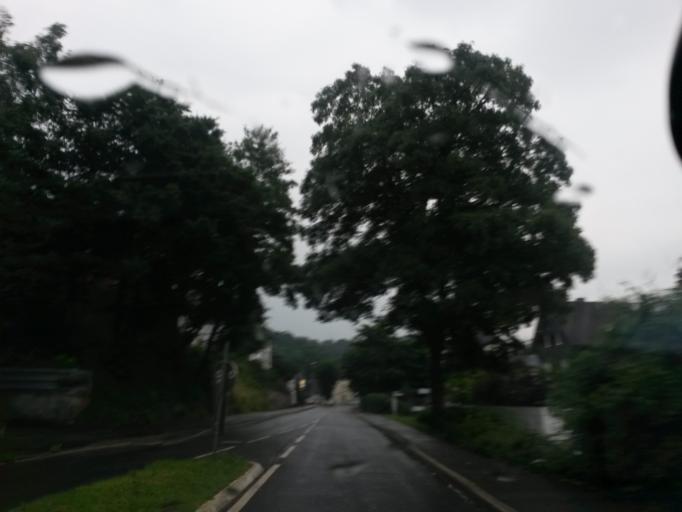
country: DE
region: North Rhine-Westphalia
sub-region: Regierungsbezirk Koln
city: Engelskirchen
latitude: 50.9930
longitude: 7.4590
